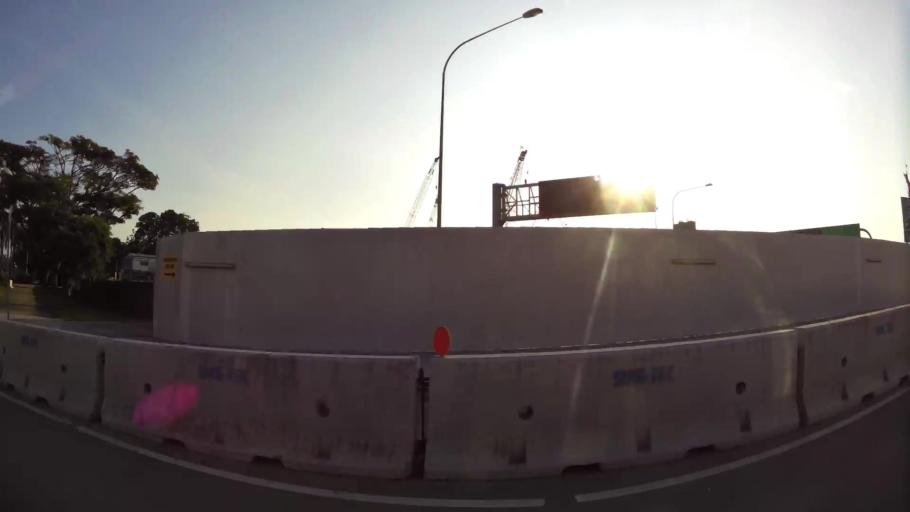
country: SG
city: Singapore
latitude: 1.2755
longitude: 103.8638
